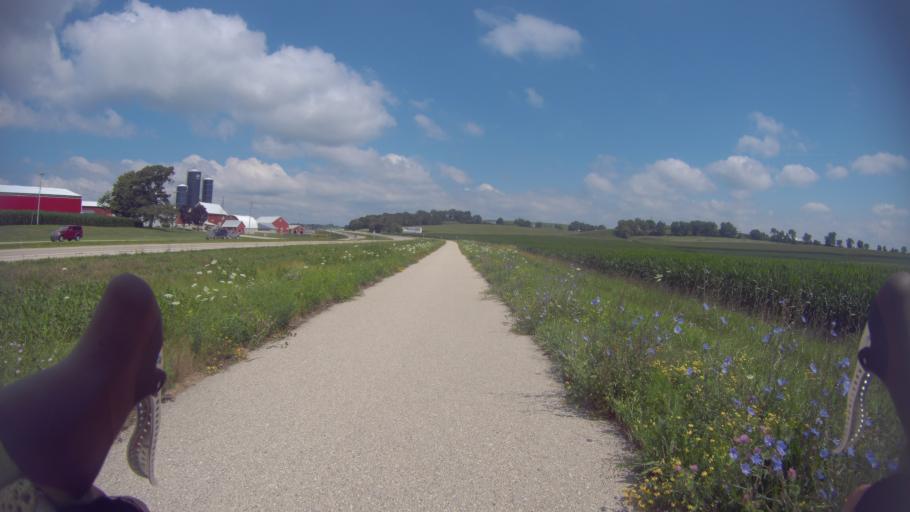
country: US
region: Wisconsin
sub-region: Dane County
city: Middleton
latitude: 43.1541
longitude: -89.5276
